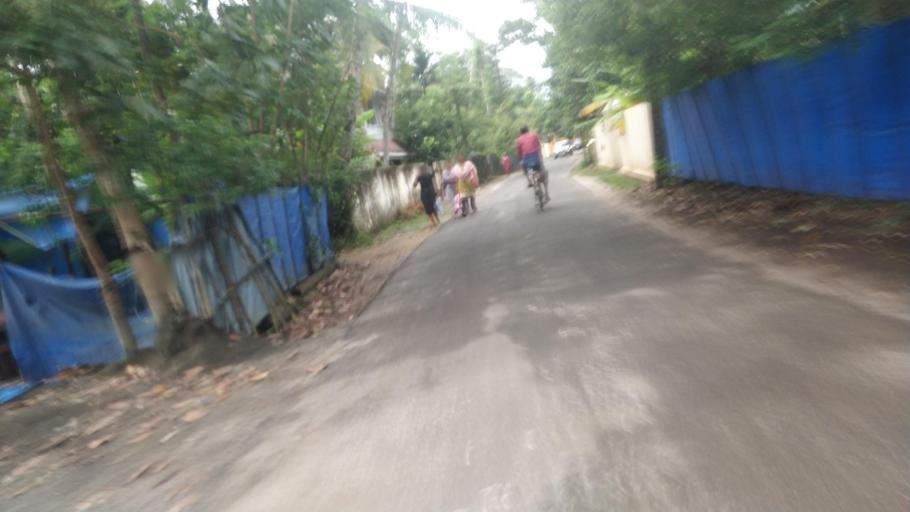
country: IN
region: Kerala
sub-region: Alappuzha
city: Vayalar
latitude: 9.7067
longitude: 76.3487
